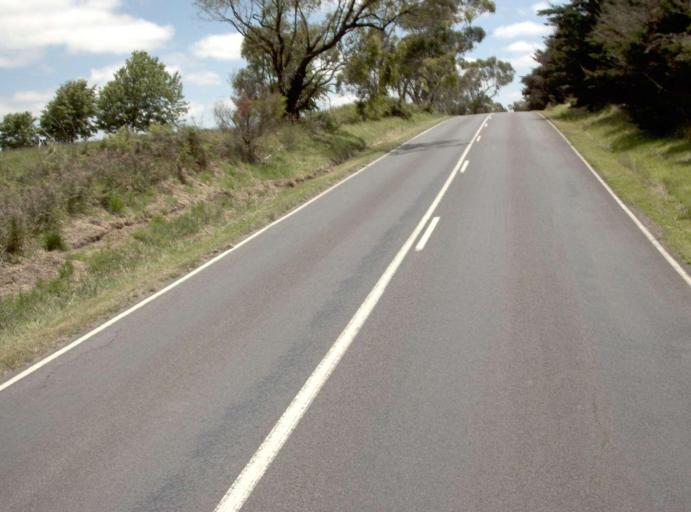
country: AU
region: Victoria
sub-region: Bass Coast
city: North Wonthaggi
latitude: -38.5990
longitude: 146.0195
